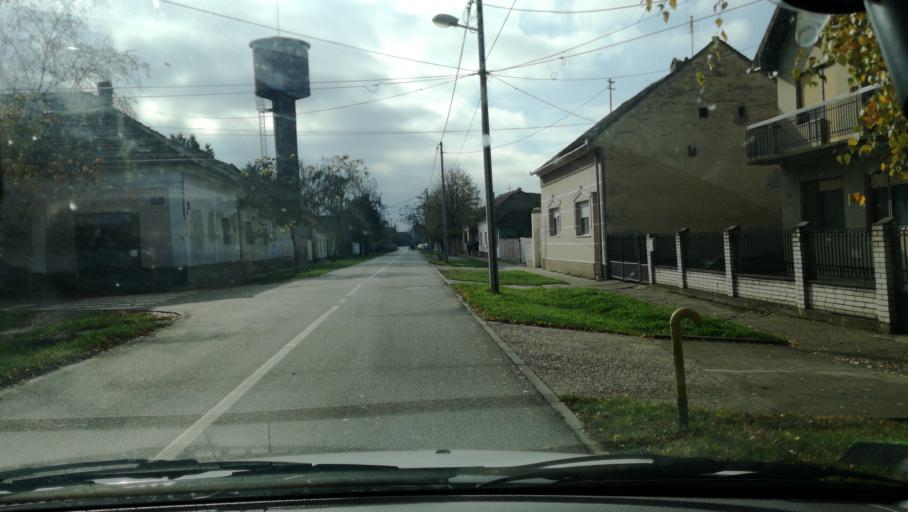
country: RS
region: Autonomna Pokrajina Vojvodina
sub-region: Severnobanatski Okrug
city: Kikinda
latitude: 45.8305
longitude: 20.4601
